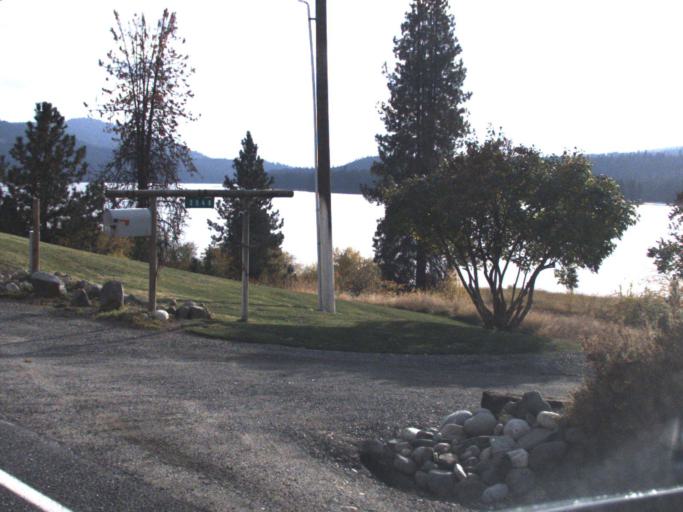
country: US
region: Washington
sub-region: Stevens County
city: Kettle Falls
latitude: 48.2843
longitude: -118.1380
